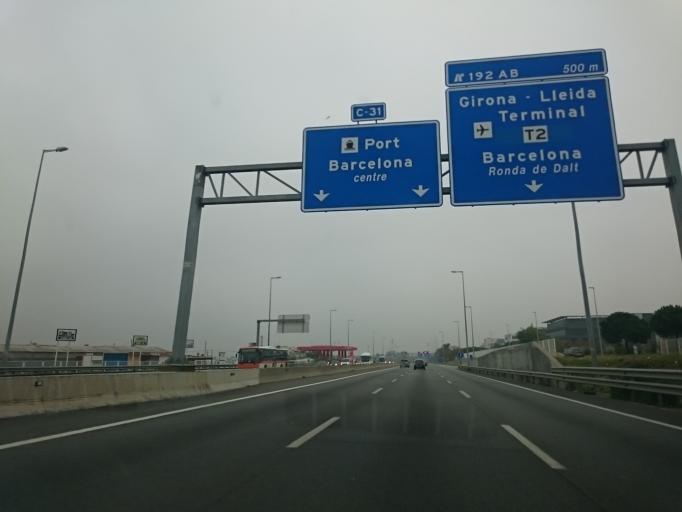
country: ES
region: Catalonia
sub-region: Provincia de Barcelona
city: El Prat de Llobregat
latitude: 41.3146
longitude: 2.0691
